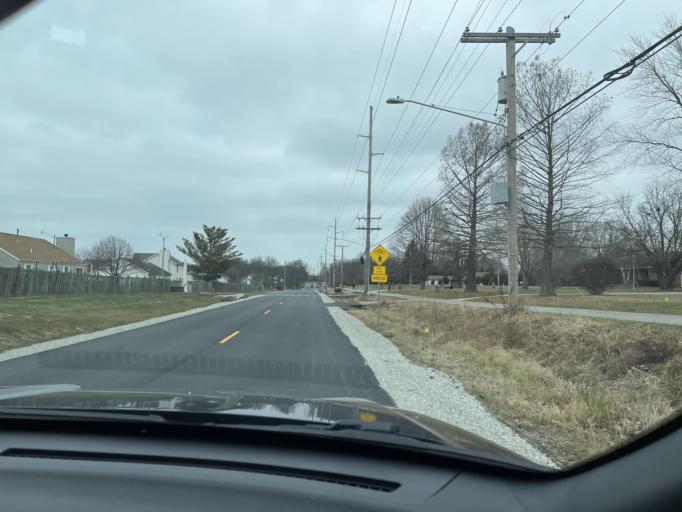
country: US
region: Illinois
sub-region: Sangamon County
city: Rochester
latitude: 39.7659
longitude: -89.5787
